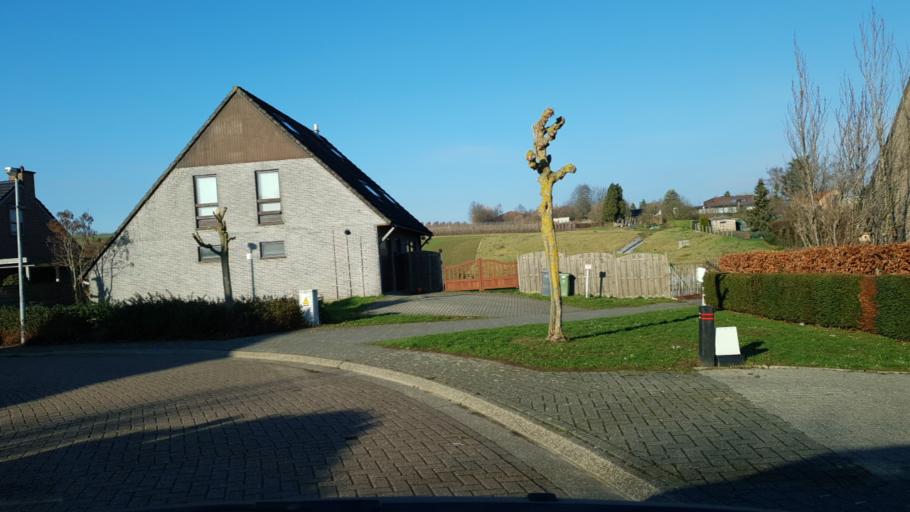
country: BE
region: Flanders
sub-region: Provincie Vlaams-Brabant
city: Bertem
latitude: 50.8732
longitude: 4.6278
